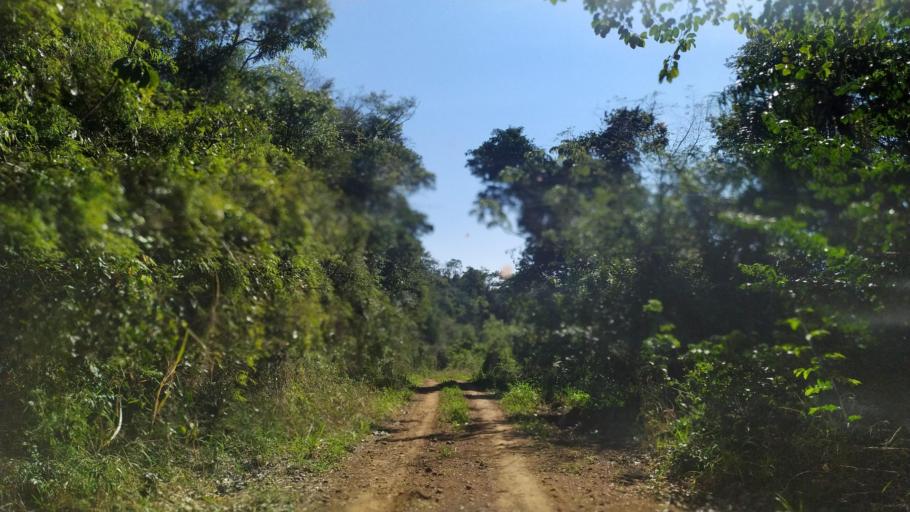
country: AR
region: Misiones
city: El Alcazar
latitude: -26.7645
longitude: -54.5768
